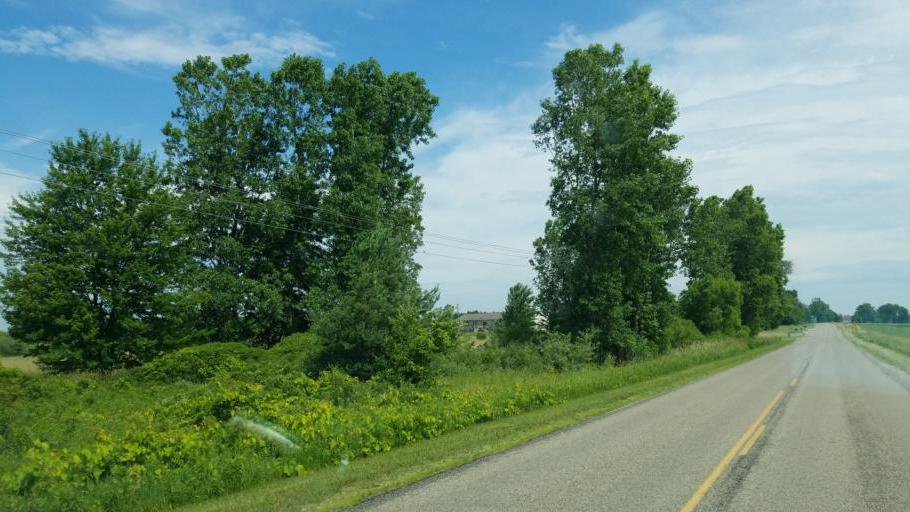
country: US
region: Michigan
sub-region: Barry County
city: Nashville
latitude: 42.6789
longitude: -85.0343
